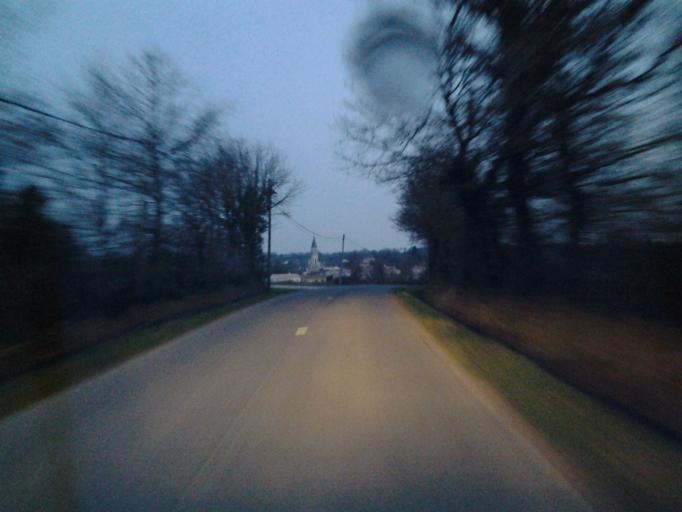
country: FR
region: Pays de la Loire
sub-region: Departement de la Vendee
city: Saint-Florent-des-Bois
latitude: 46.5698
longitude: -1.3384
